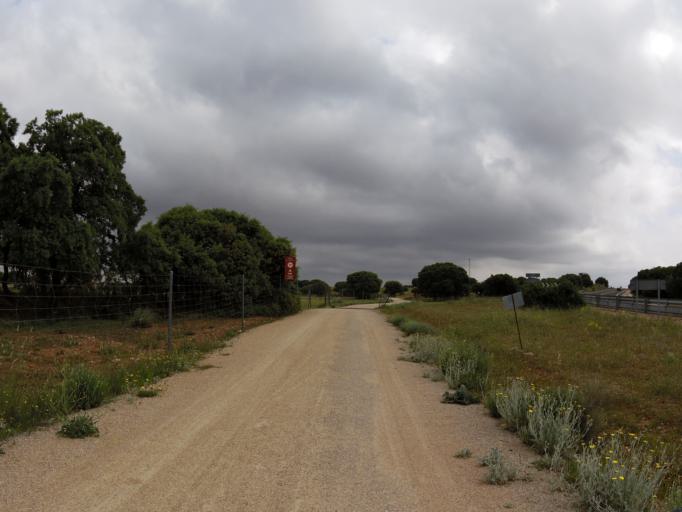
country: ES
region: Castille-La Mancha
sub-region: Provincia de Albacete
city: Robledo
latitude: 38.7352
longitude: -2.4668
